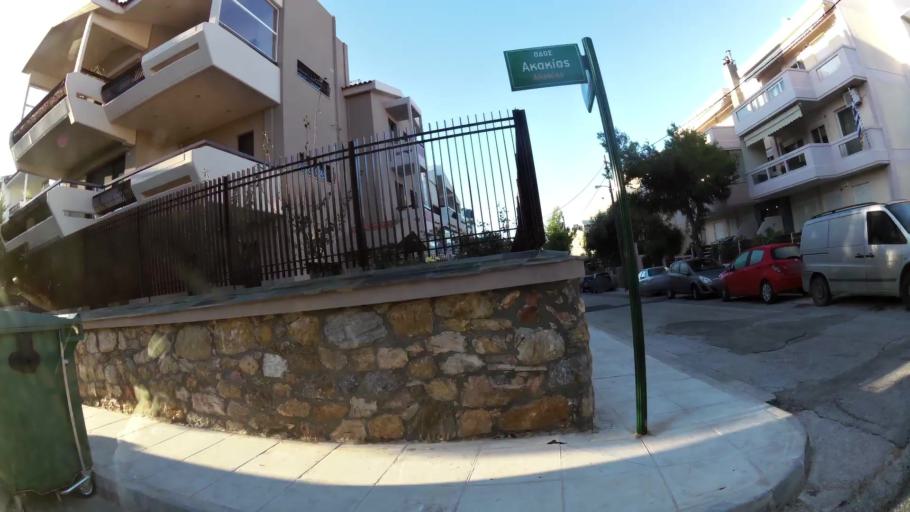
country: GR
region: Attica
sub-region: Nomarchia Anatolikis Attikis
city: Gerakas
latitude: 38.0341
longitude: 23.8539
